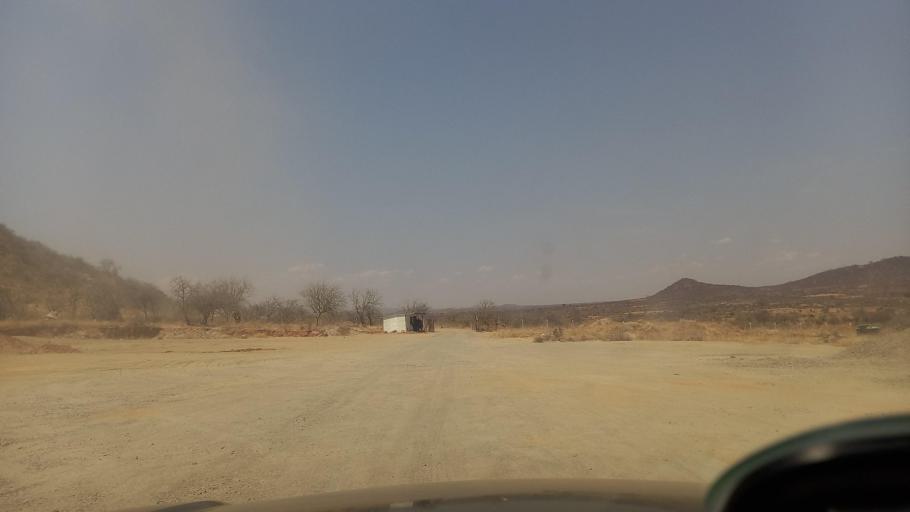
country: TZ
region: Dodoma
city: Msanga
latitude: -6.1799
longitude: 36.0701
